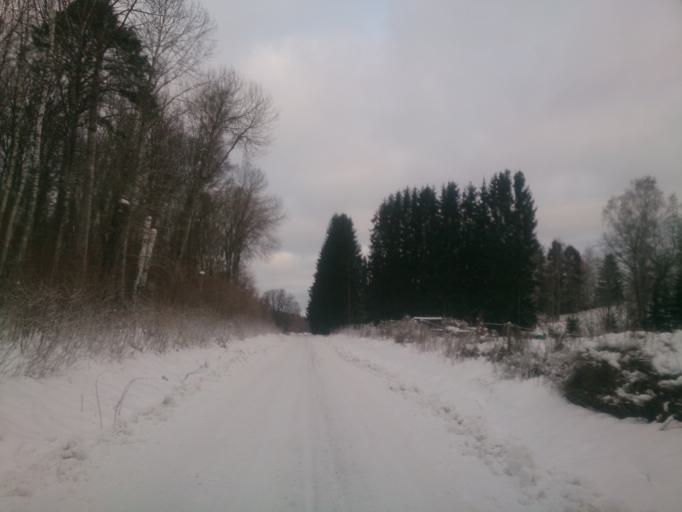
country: SE
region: OEstergoetland
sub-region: Atvidabergs Kommun
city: Atvidaberg
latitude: 58.2185
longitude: 15.9899
